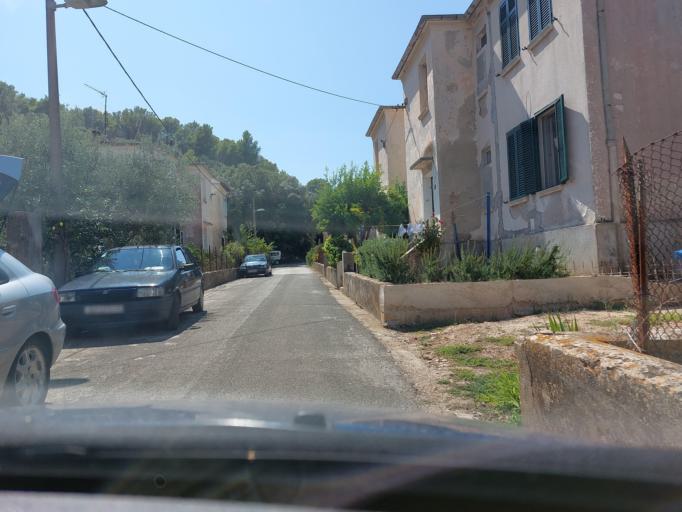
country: HR
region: Dubrovacko-Neretvanska
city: Smokvica
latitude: 42.7425
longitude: 16.8270
